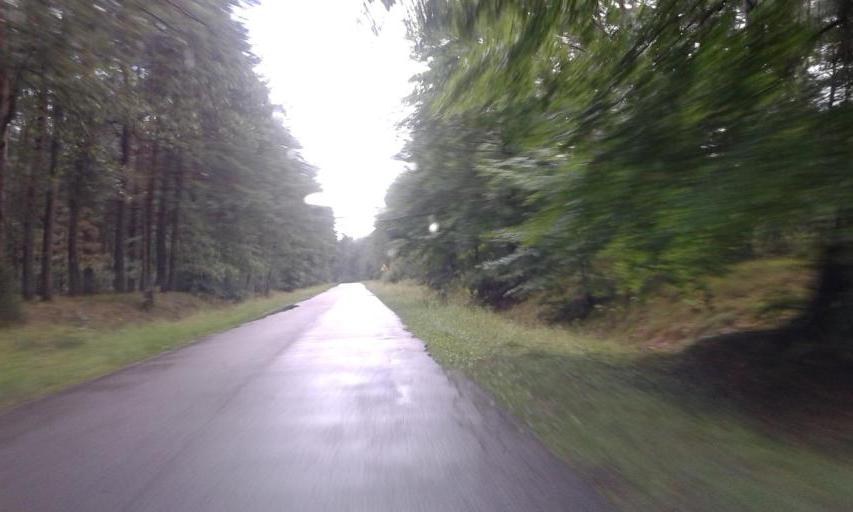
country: PL
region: West Pomeranian Voivodeship
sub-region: Powiat szczecinecki
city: Borne Sulinowo
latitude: 53.5498
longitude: 16.5142
